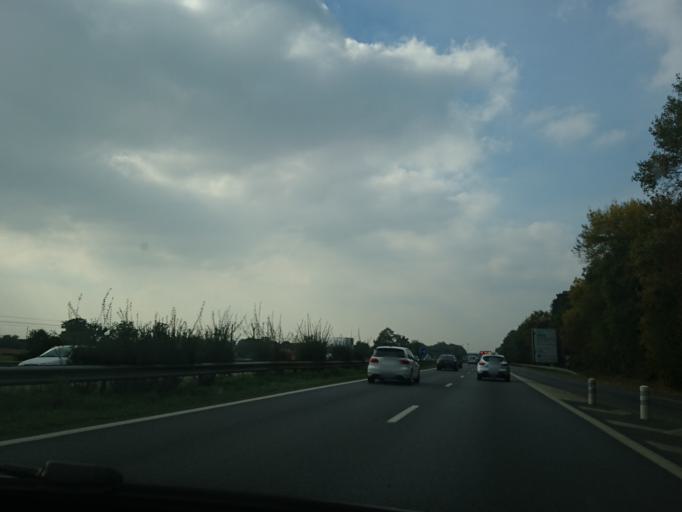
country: FR
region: Brittany
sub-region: Departement d'Ille-et-Vilaine
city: Rennes
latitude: 48.0816
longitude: -1.6533
